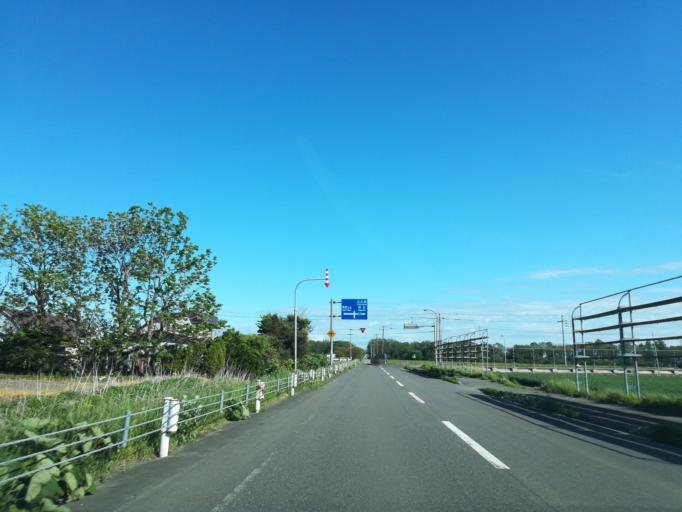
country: JP
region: Hokkaido
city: Ebetsu
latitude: 43.0588
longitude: 141.6176
